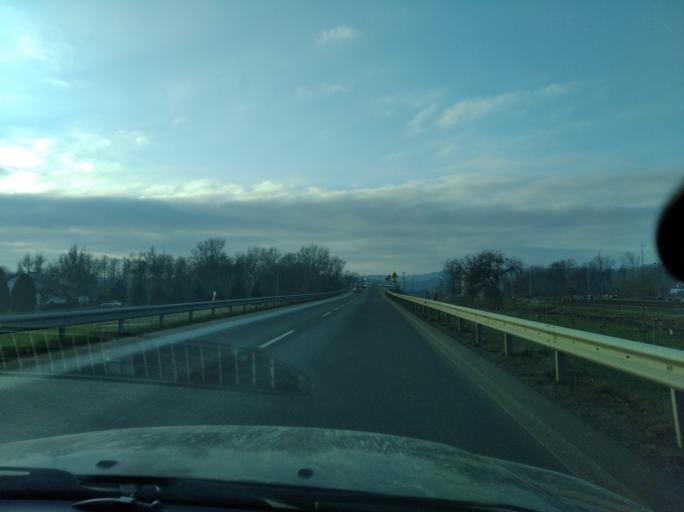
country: PL
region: Subcarpathian Voivodeship
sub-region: Powiat strzyzowski
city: Czudec
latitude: 49.9405
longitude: 21.8301
